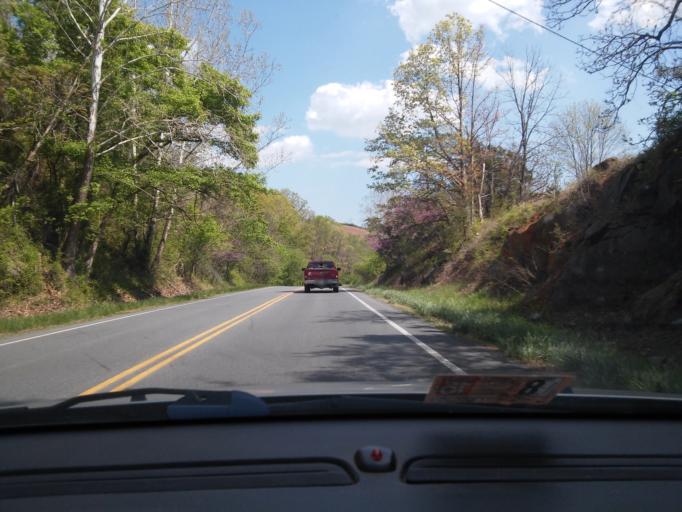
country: US
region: Virginia
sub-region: Warren County
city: Front Royal
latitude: 38.8941
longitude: -78.1775
